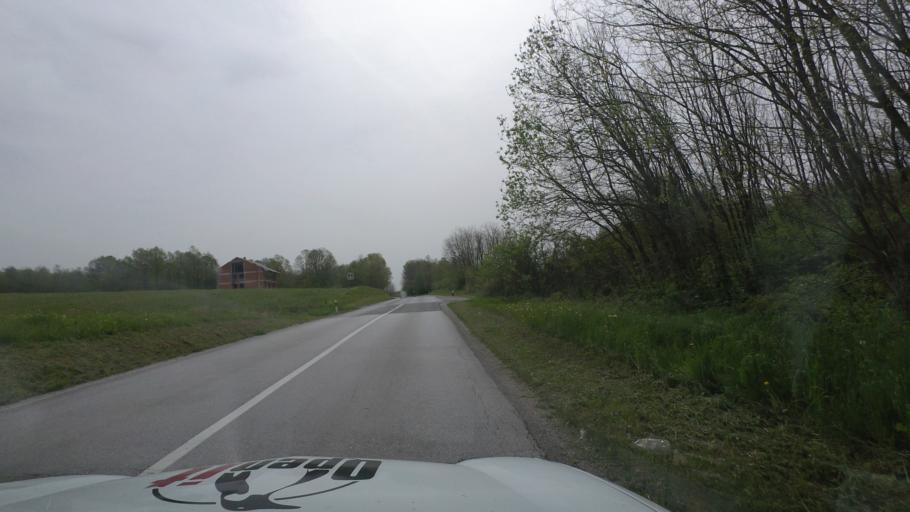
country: HR
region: Sisacko-Moslavacka
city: Gvozd
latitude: 45.3456
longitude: 15.8875
